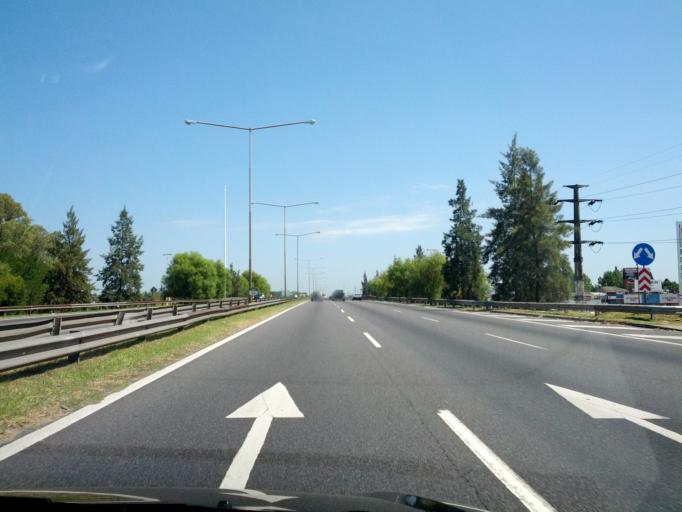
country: AR
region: Buenos Aires
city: Santa Catalina - Dique Lujan
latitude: -34.3966
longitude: -58.7390
